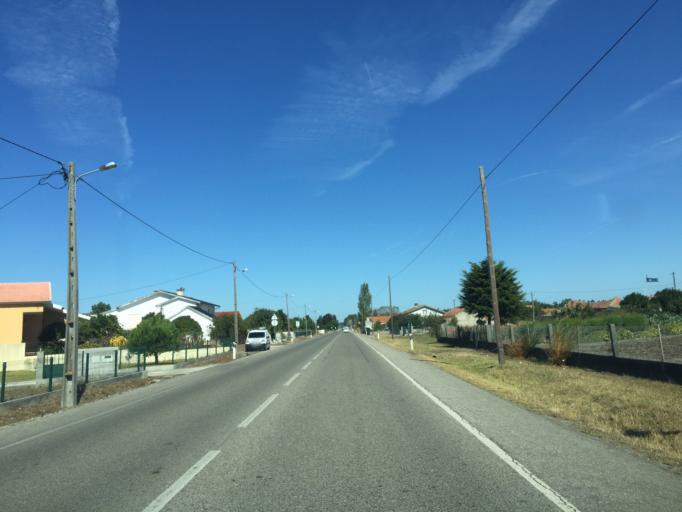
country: PT
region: Coimbra
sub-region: Figueira da Foz
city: Alhadas
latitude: 40.2322
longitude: -8.7988
